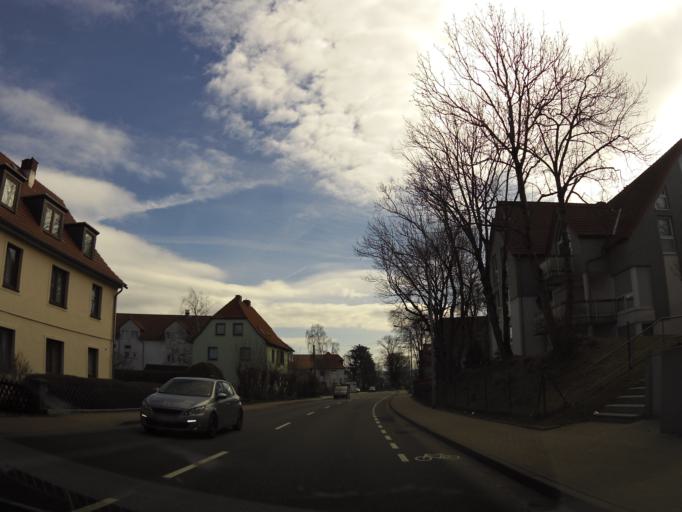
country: DE
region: Thuringia
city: Ilmenau
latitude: 50.6899
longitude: 10.9068
